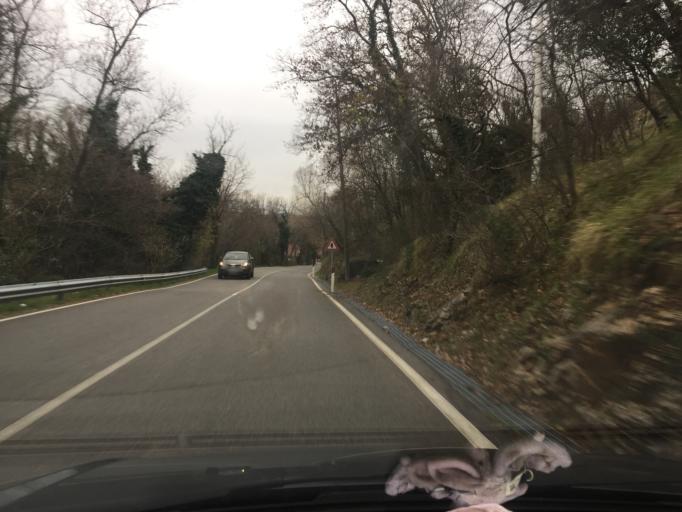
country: IT
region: Friuli Venezia Giulia
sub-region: Provincia di Trieste
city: Zolla
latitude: 45.7143
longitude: 13.8082
